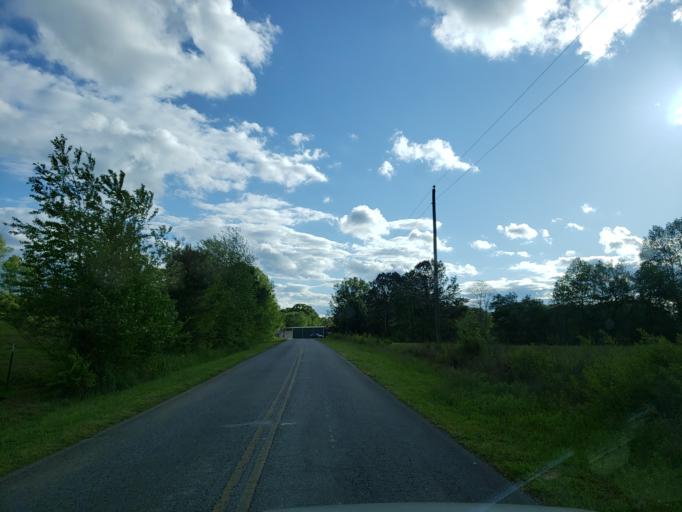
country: US
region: Georgia
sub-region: Haralson County
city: Tallapoosa
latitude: 33.8115
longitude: -85.2916
